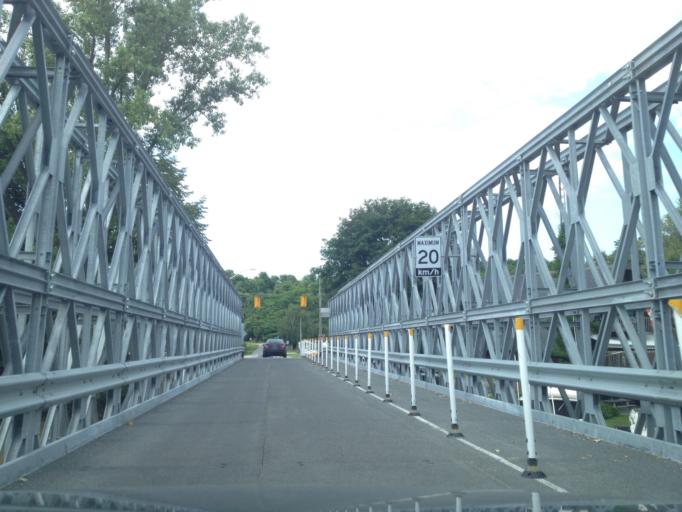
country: CA
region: Ontario
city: Aylmer
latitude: 42.6608
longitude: -81.0133
